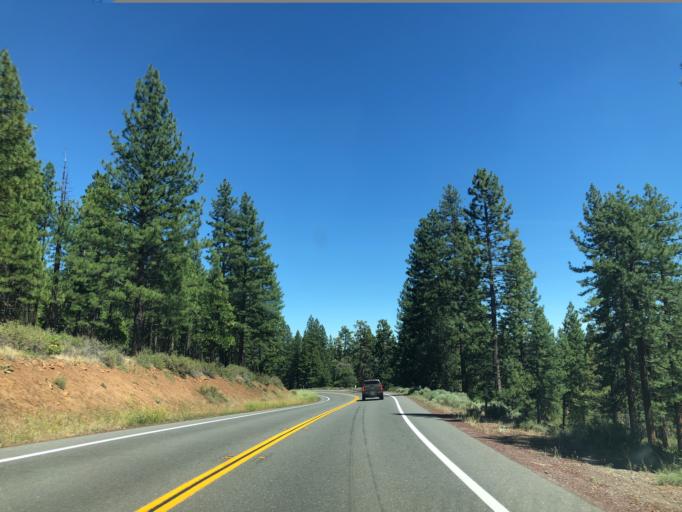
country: US
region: California
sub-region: Lassen County
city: Susanville
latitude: 40.4175
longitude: -120.7786
